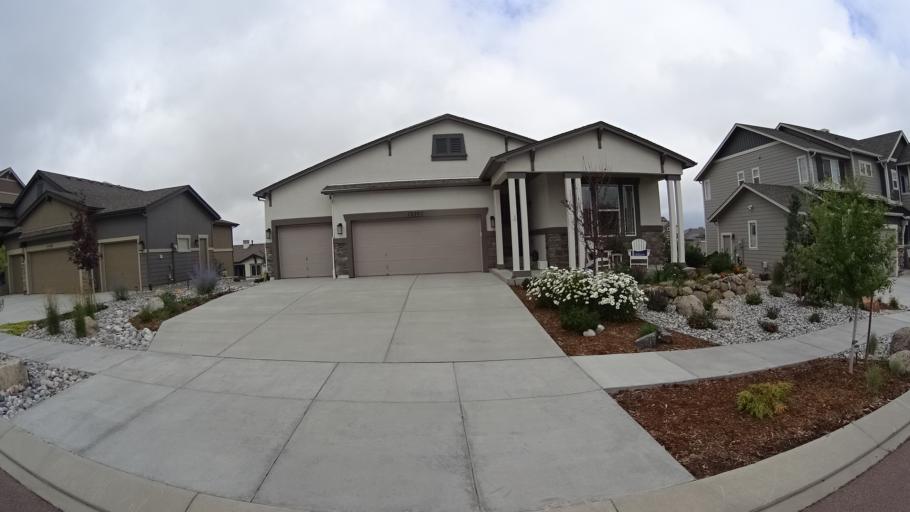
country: US
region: Colorado
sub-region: El Paso County
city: Gleneagle
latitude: 39.0124
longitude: -104.7902
